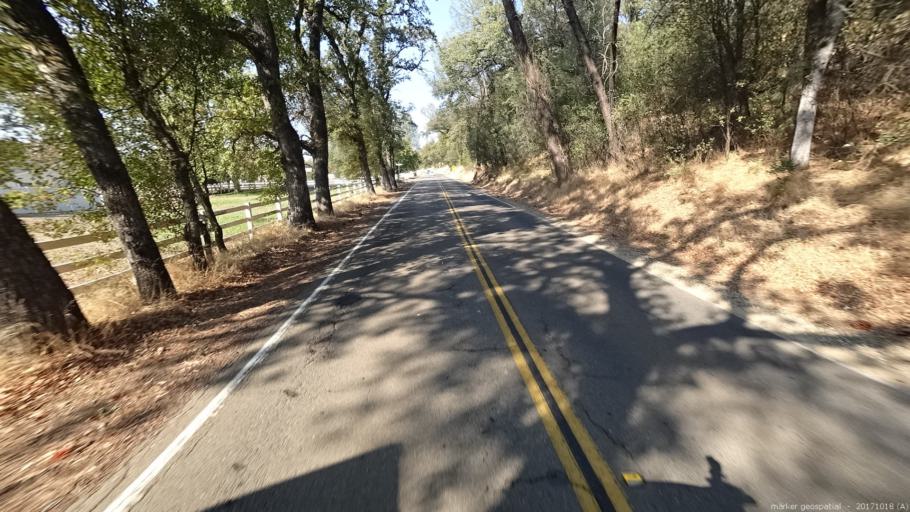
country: US
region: California
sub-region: Shasta County
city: Palo Cedro
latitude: 40.5616
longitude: -122.2846
